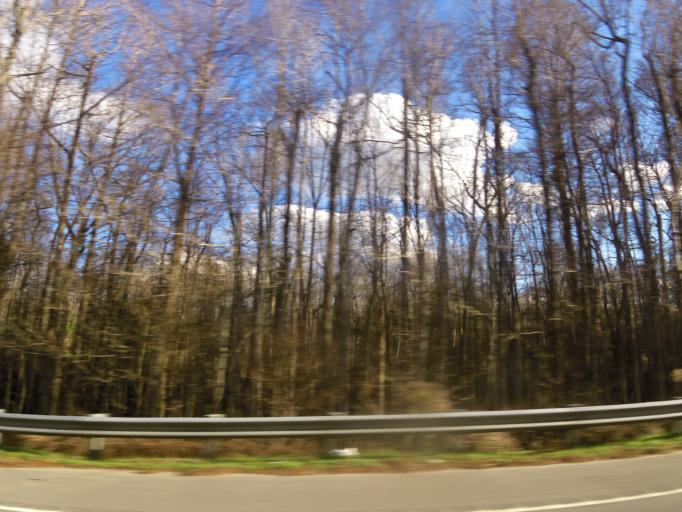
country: US
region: South Carolina
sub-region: Clarendon County
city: Manning
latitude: 33.7127
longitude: -80.2013
